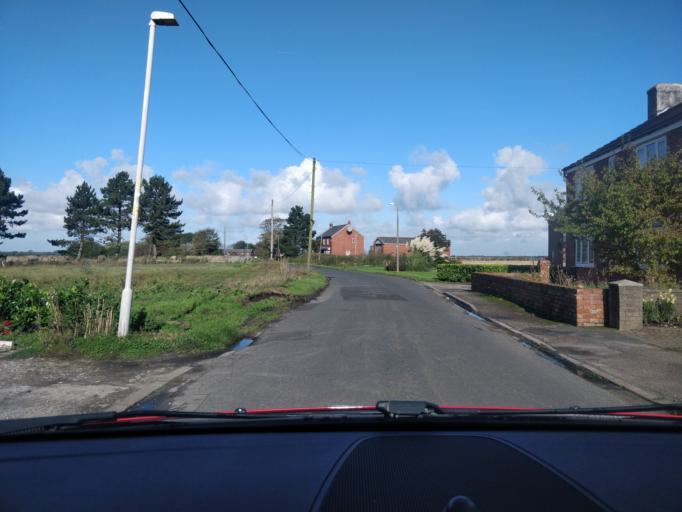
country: GB
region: England
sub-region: Lancashire
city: Banks
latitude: 53.6222
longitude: -2.9390
